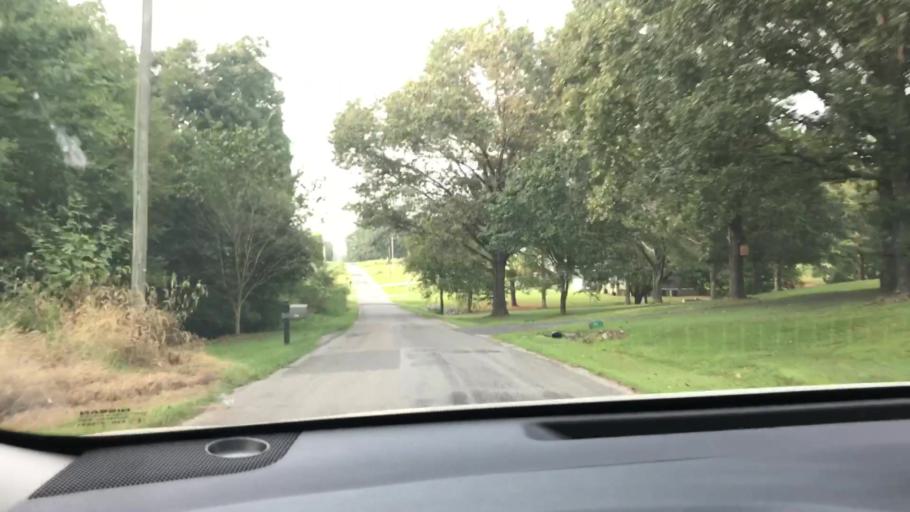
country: US
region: Kentucky
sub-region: Calloway County
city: Murray
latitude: 36.5722
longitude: -88.2200
